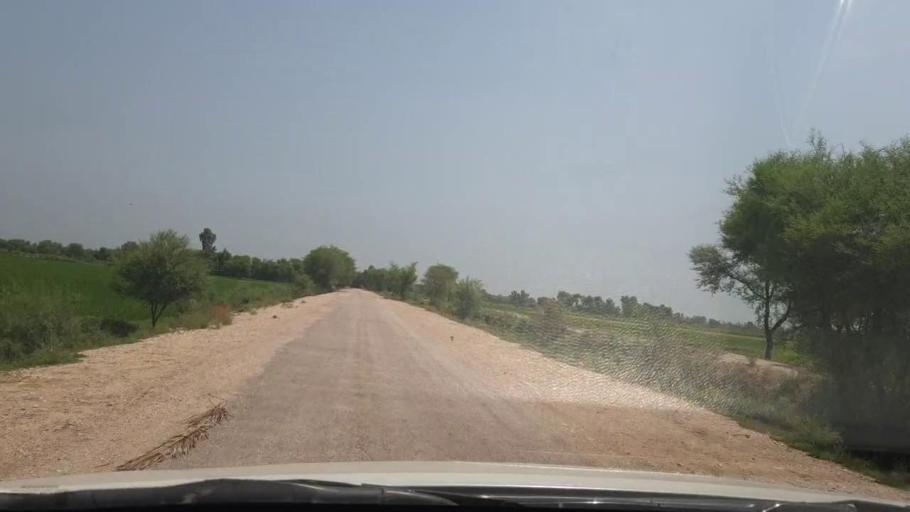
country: PK
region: Sindh
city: Rustam jo Goth
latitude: 28.0296
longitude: 68.7582
